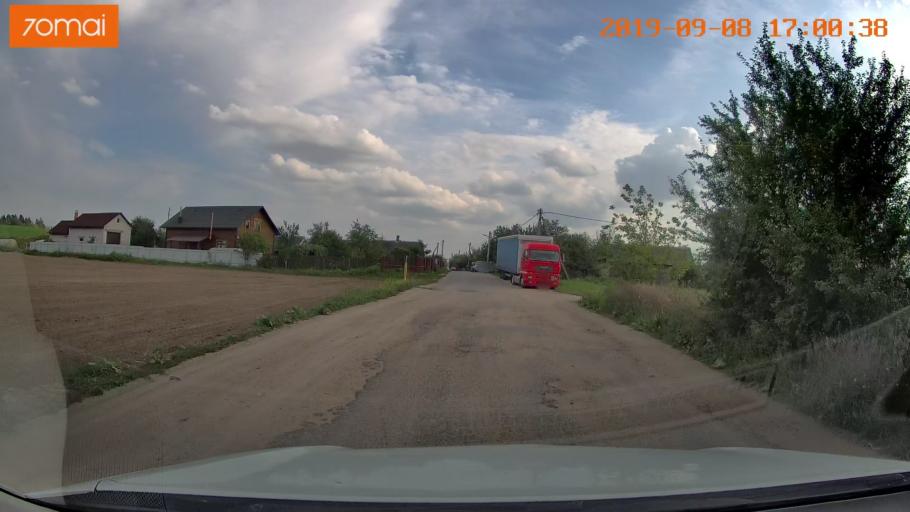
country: BY
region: Grodnenskaya
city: Hrodna
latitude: 53.7142
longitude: 23.9327
